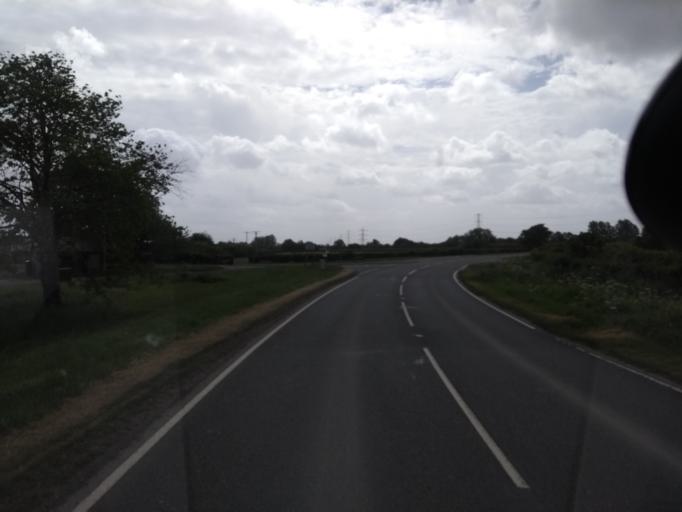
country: GB
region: England
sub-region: Somerset
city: Bridgwater
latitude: 51.1730
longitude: -3.0690
